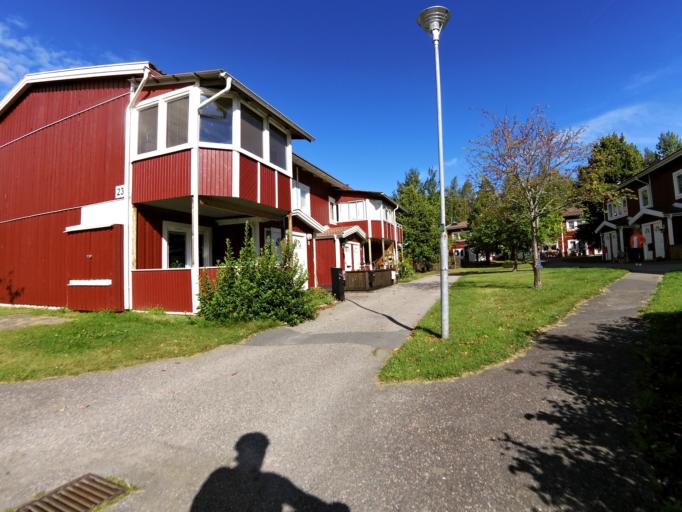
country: SE
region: Gaevleborg
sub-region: Gavle Kommun
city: Gavle
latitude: 60.6647
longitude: 17.2179
